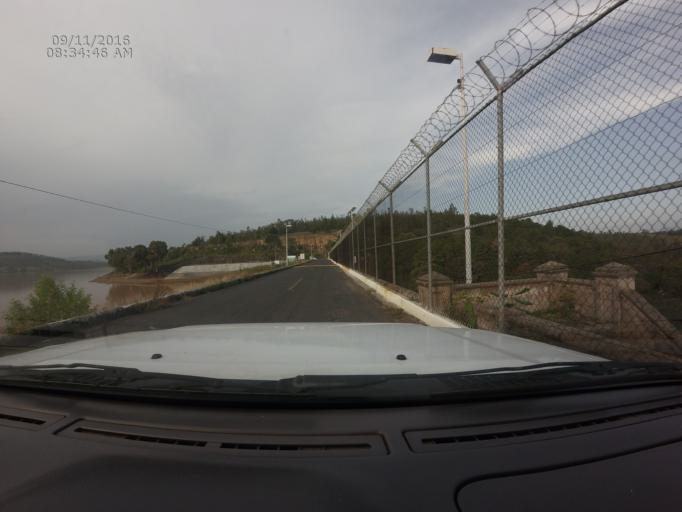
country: MX
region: Michoacan
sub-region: Morelia
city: Morelos
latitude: 19.6299
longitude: -101.2592
